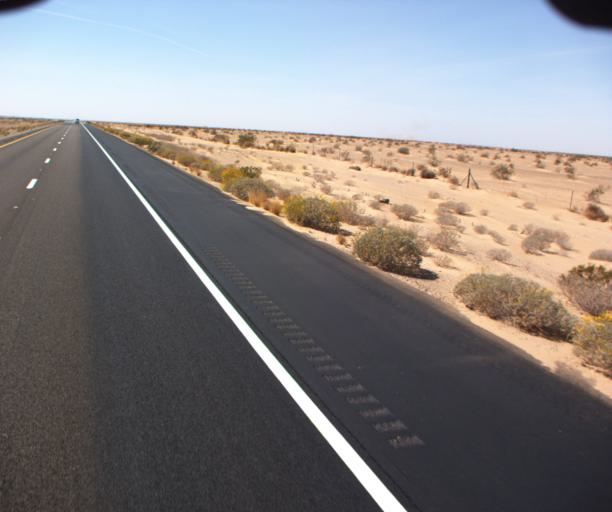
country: US
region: Arizona
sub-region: Yuma County
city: Somerton
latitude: 32.4953
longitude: -114.5764
